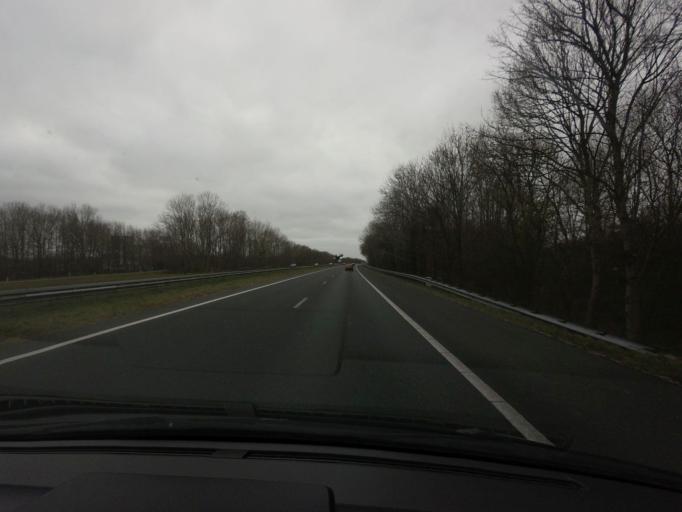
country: NL
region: Groningen
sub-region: Gemeente Hoogezand-Sappemeer
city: Hoogezand
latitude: 53.1693
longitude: 6.7619
